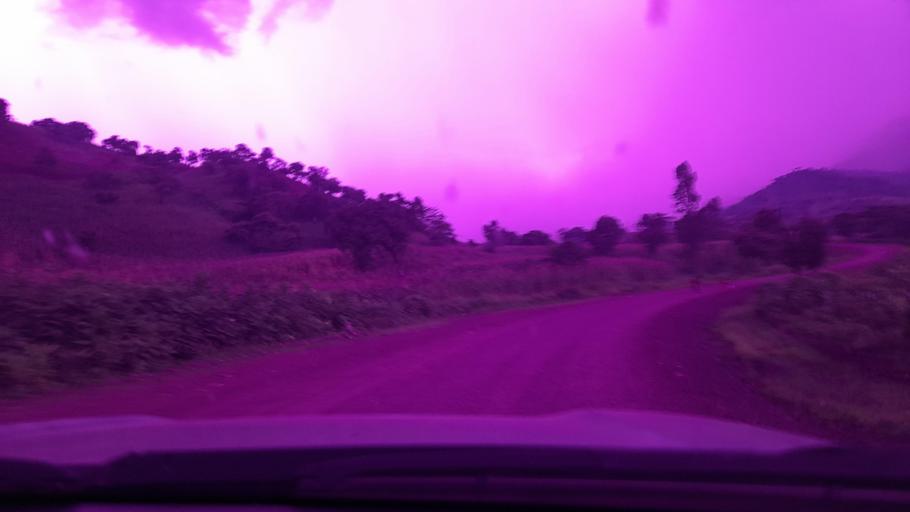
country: ET
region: Southern Nations, Nationalities, and People's Region
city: Mizan Teferi
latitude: 6.7352
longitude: 35.8638
